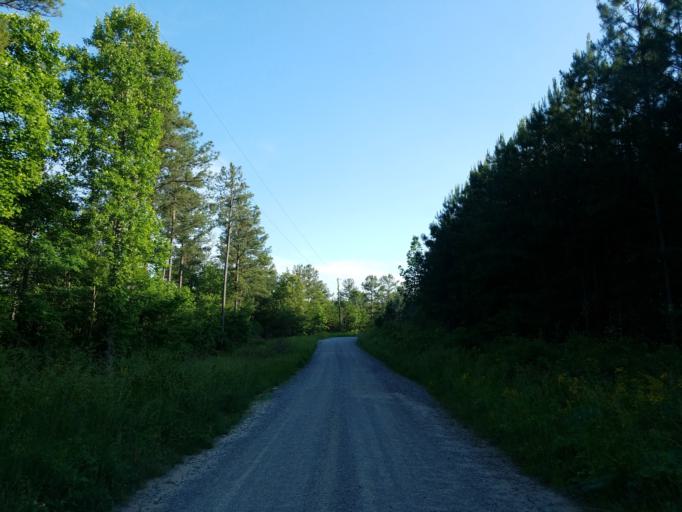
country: US
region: Georgia
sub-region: Pickens County
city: Nelson
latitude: 34.3628
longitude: -84.3255
